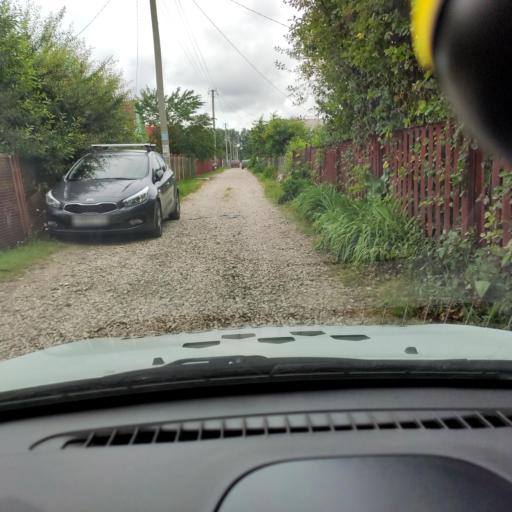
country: RU
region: Samara
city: Tol'yatti
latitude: 53.5972
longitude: 49.2904
